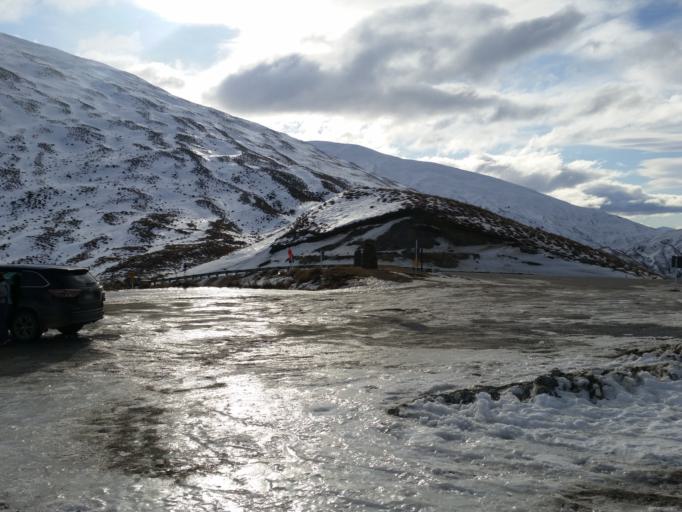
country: NZ
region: Otago
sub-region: Queenstown-Lakes District
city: Arrowtown
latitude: -44.9928
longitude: 168.9387
